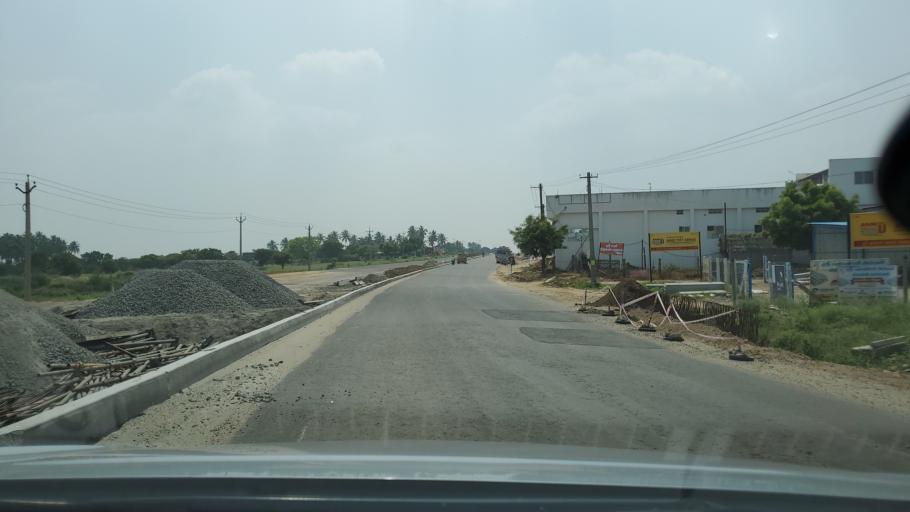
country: IN
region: Tamil Nadu
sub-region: Tiruppur
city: Kangayam
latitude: 10.9354
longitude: 77.4419
